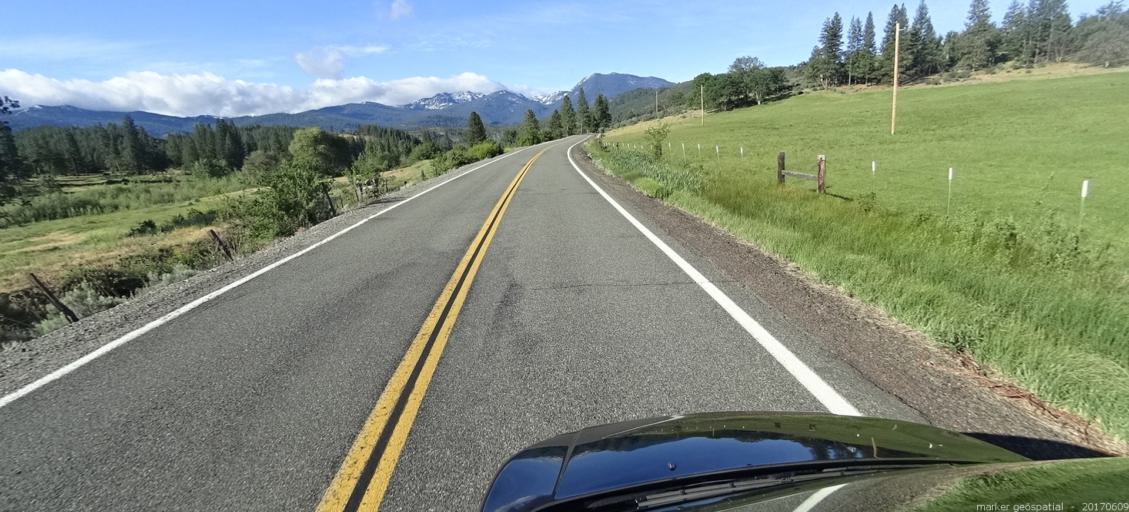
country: US
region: California
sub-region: Siskiyou County
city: Weed
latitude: 41.3602
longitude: -122.7186
